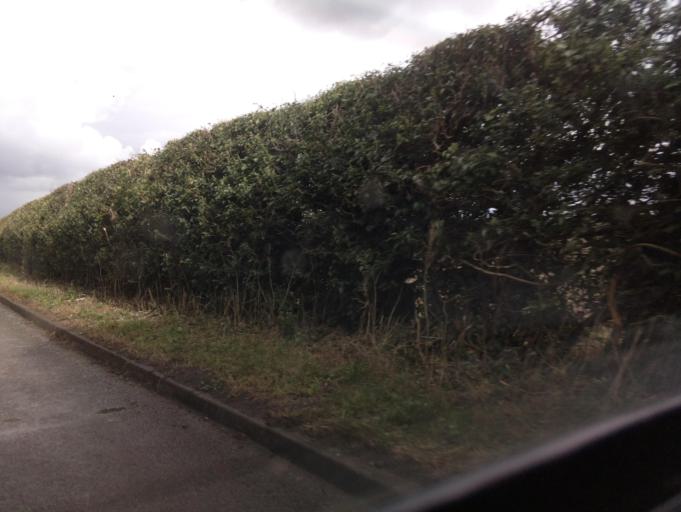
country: GB
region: England
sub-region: Staffordshire
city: Eccleshall
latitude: 52.8796
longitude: -2.2386
